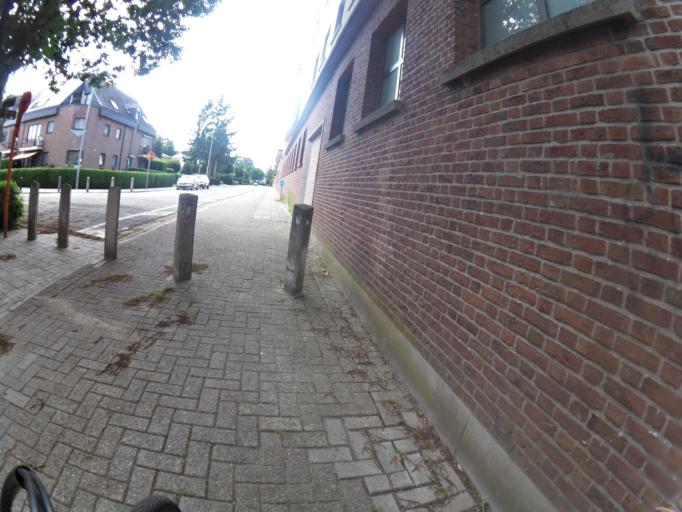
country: BE
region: Flanders
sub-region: Provincie Antwerpen
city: Mol
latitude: 51.1861
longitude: 5.1081
